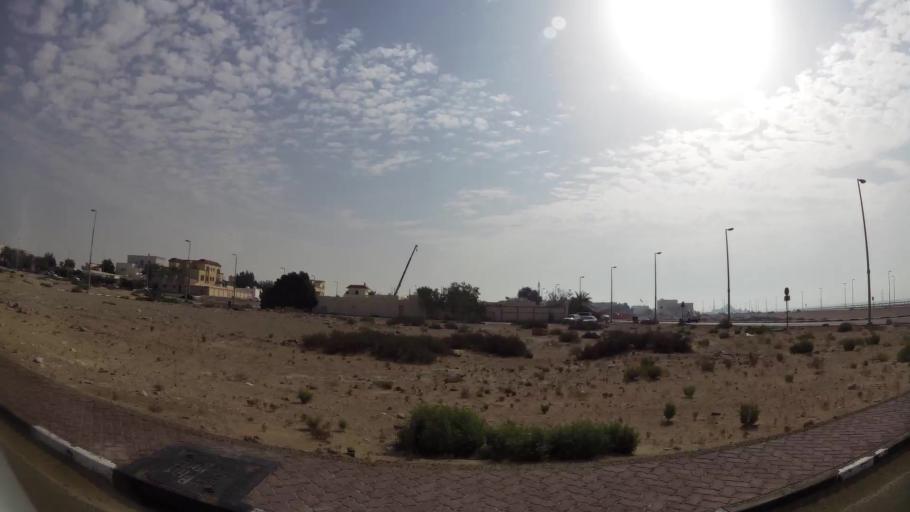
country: AE
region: Abu Dhabi
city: Abu Dhabi
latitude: 24.2636
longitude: 54.6906
